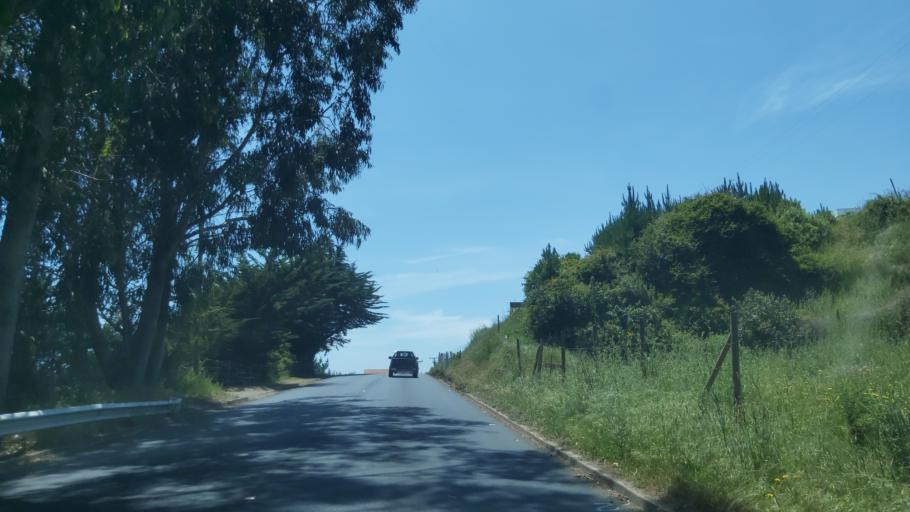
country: CL
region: Maule
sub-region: Provincia de Cauquenes
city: Cauquenes
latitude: -35.8281
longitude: -72.6145
